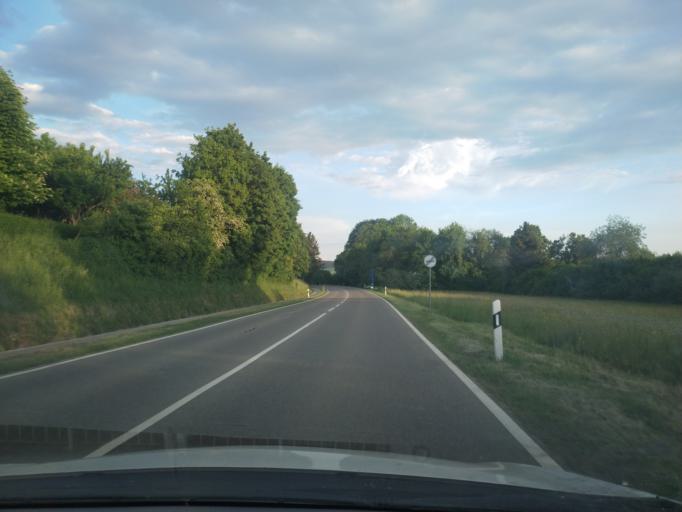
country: DE
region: Baden-Wuerttemberg
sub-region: Freiburg Region
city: Bonndorf im Schwarzwald
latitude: 47.8137
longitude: 8.3437
